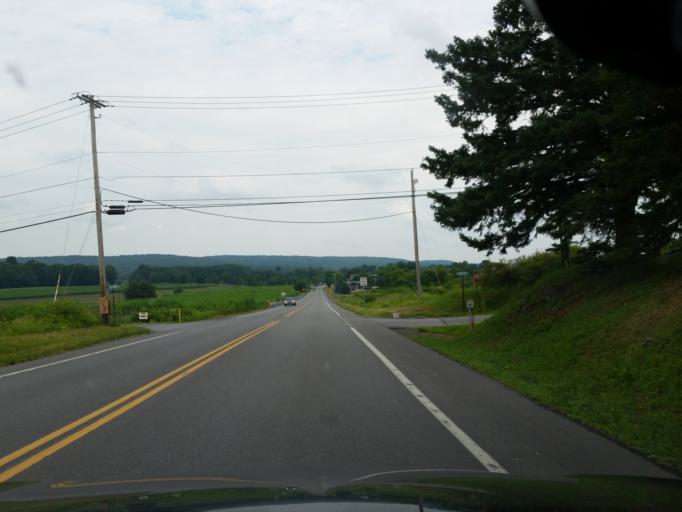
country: US
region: Pennsylvania
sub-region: Centre County
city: Zion
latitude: 40.9127
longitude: -77.6802
